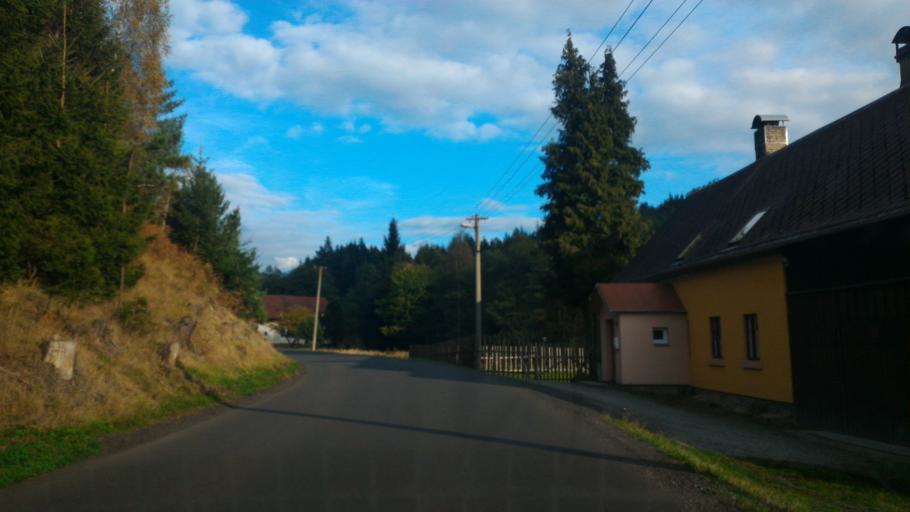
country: CZ
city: Kamenicky Senov
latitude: 50.8095
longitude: 14.4805
